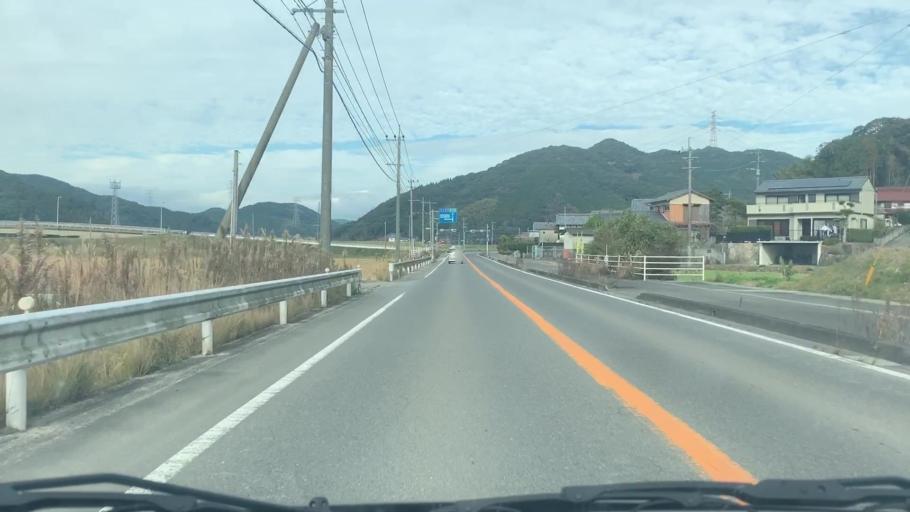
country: JP
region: Saga Prefecture
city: Karatsu
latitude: 33.3733
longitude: 130.0018
